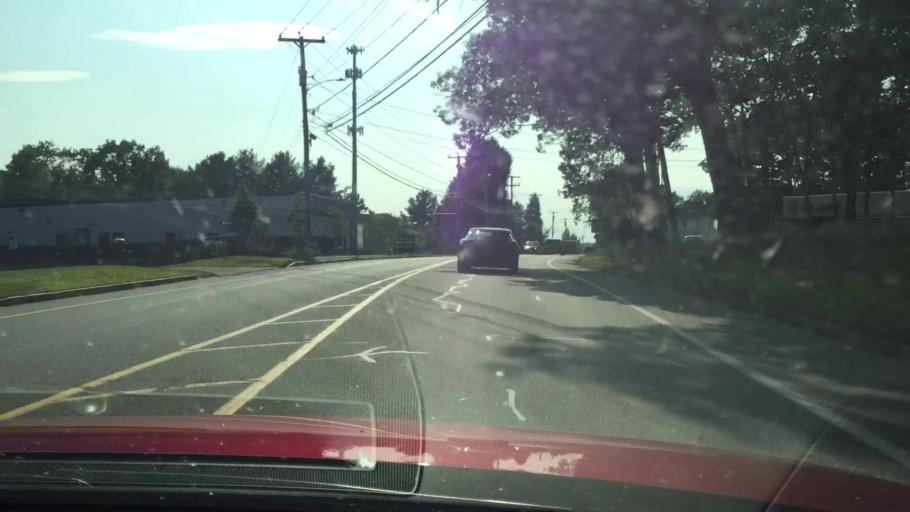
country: US
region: Maine
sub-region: Cumberland County
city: South Portland Gardens
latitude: 43.6884
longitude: -70.3015
